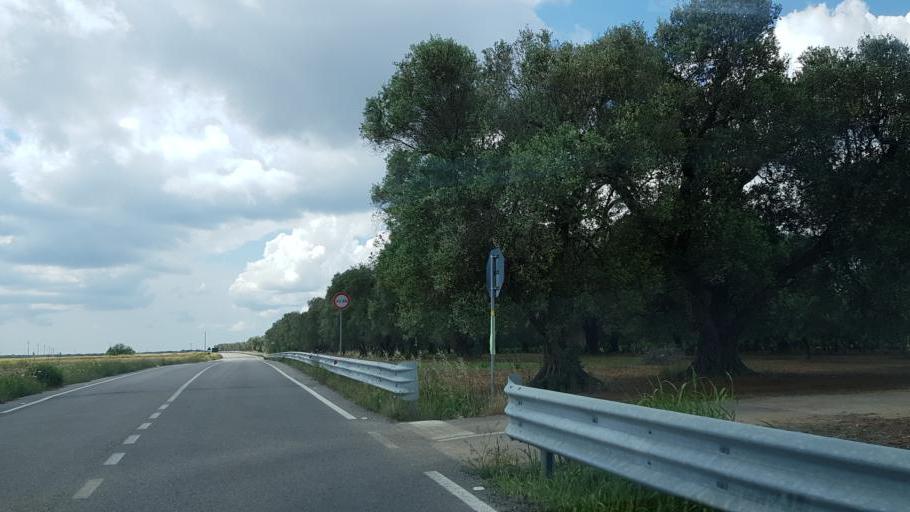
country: IT
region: Apulia
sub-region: Provincia di Brindisi
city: Mesagne
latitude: 40.5099
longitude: 17.8271
